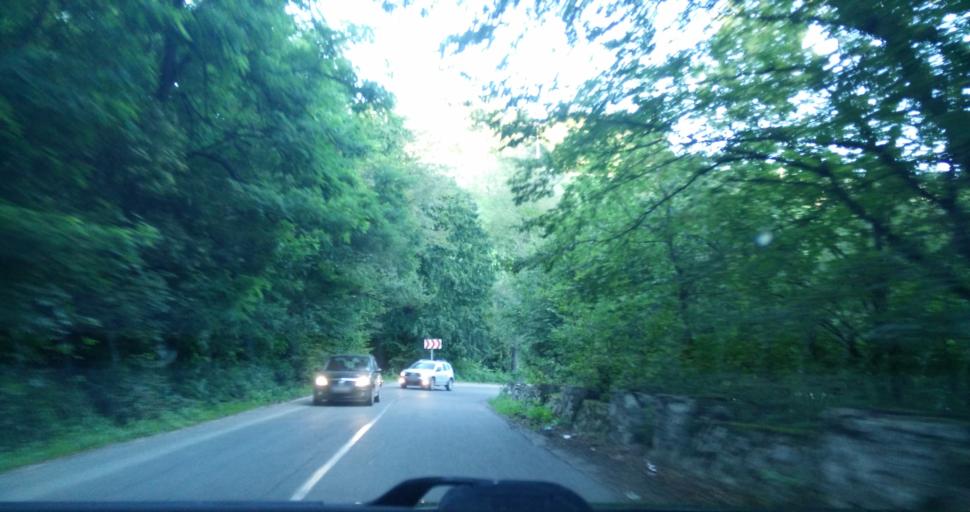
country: RO
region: Bihor
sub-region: Oras Nucet
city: Nucet
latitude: 46.4896
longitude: 22.6106
